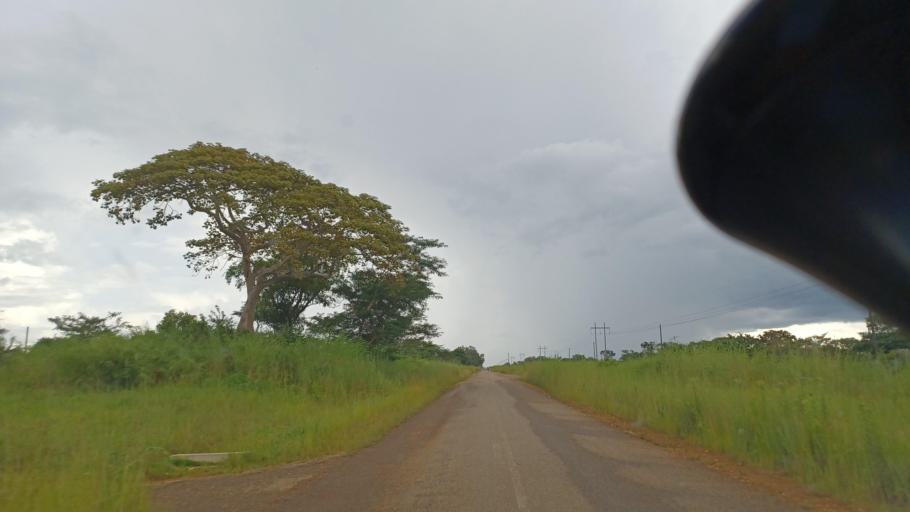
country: ZM
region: North-Western
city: Kasempa
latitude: -13.0138
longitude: 26.0029
